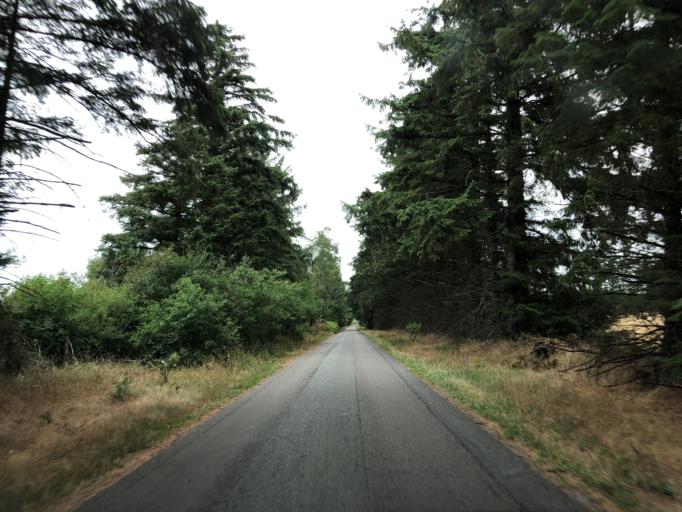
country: DK
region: Central Jutland
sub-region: Holstebro Kommune
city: Ulfborg
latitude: 56.2164
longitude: 8.3197
